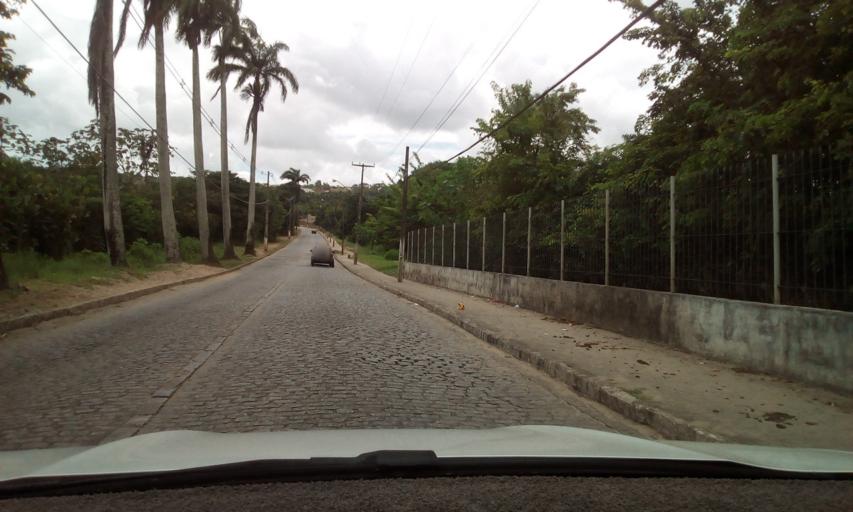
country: BR
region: Paraiba
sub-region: Rio Tinto
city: Rio Tinto
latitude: -6.8048
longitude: -35.0756
